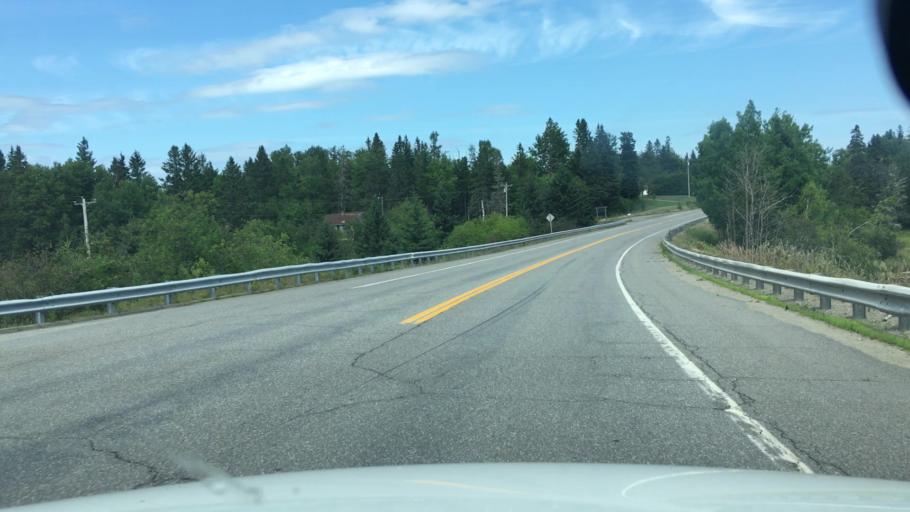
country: CA
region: New Brunswick
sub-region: Charlotte County
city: Saint Andrews
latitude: 45.0576
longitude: -67.1186
